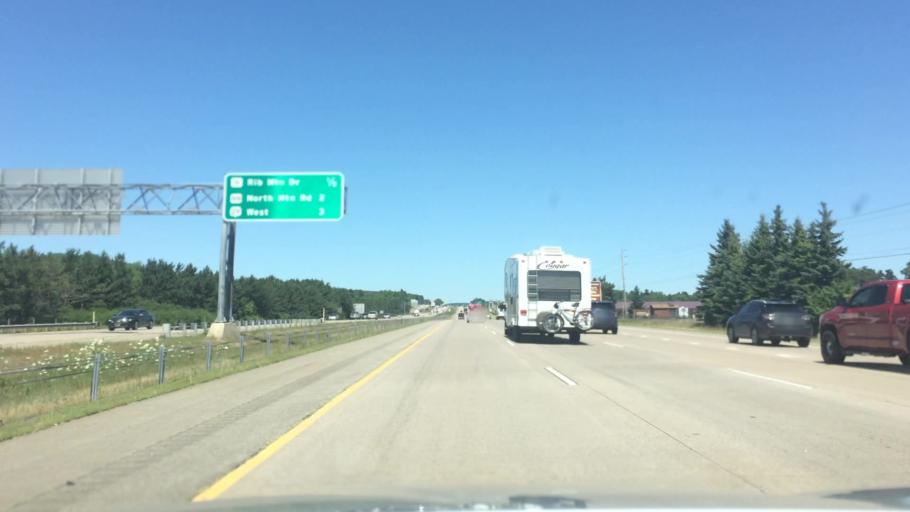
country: US
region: Wisconsin
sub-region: Marathon County
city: Rothschild
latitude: 44.9028
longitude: -89.6443
